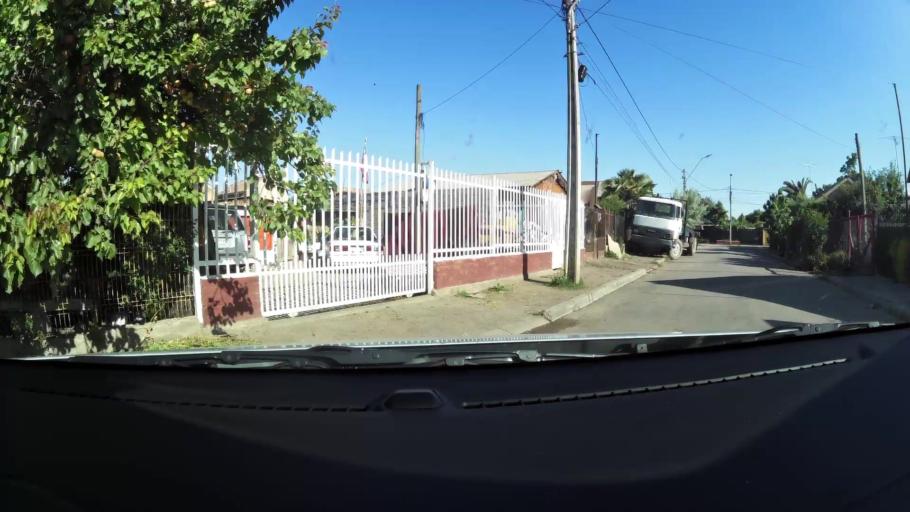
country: CL
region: Santiago Metropolitan
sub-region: Provincia de Maipo
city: San Bernardo
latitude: -33.6450
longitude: -70.6936
